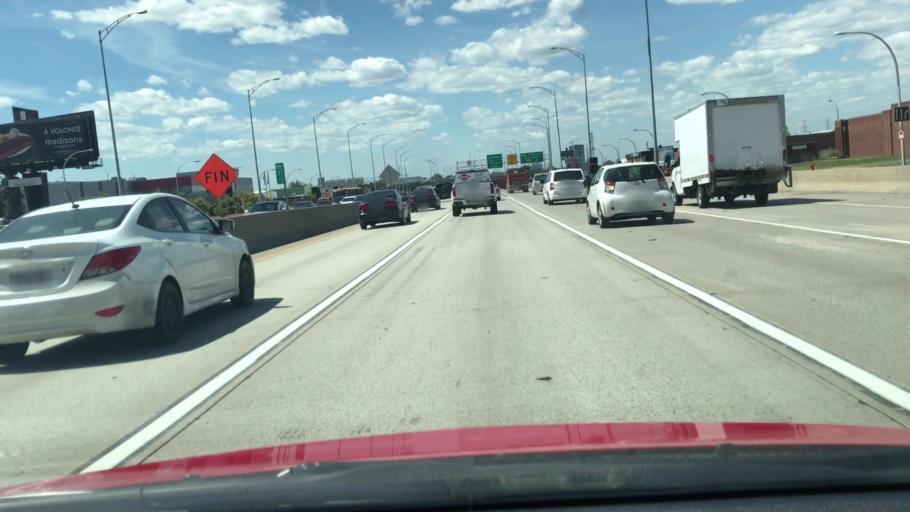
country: CA
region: Quebec
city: Dorval
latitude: 45.4959
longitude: -73.7451
